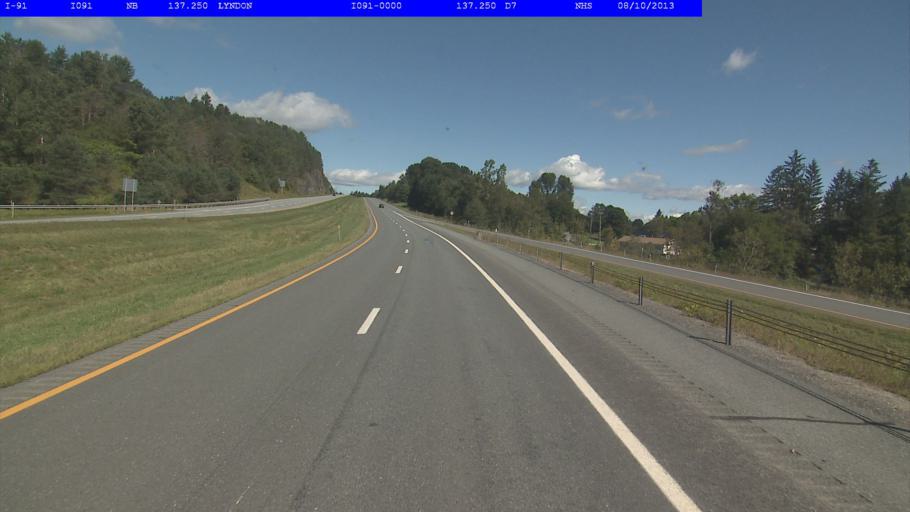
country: US
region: Vermont
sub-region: Caledonia County
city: Lyndon
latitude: 44.5185
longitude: -72.0067
